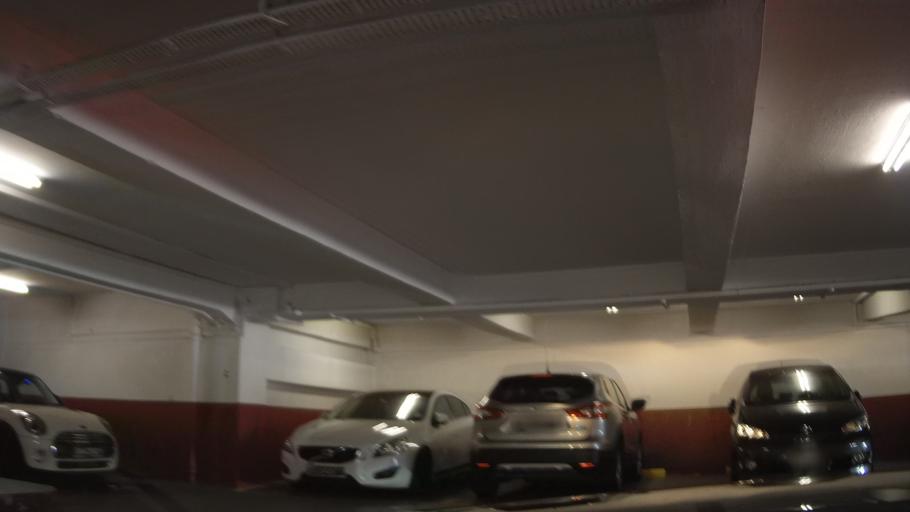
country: SG
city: Singapore
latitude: 1.2984
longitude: 103.8323
